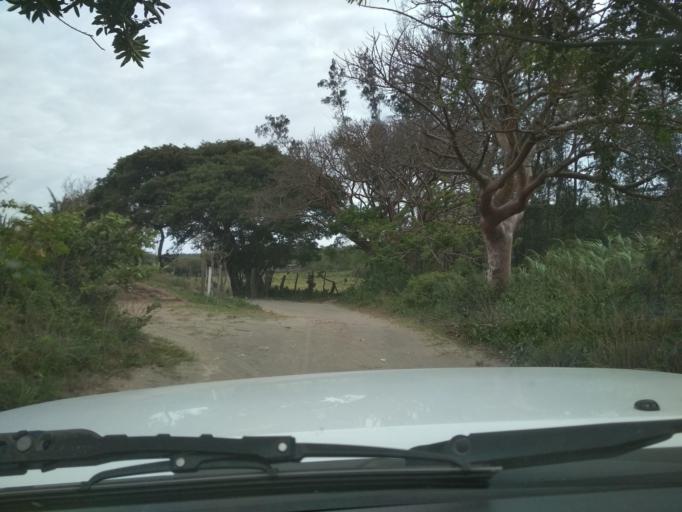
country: MX
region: Veracruz
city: Anton Lizardo
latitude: 19.0526
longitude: -95.9902
